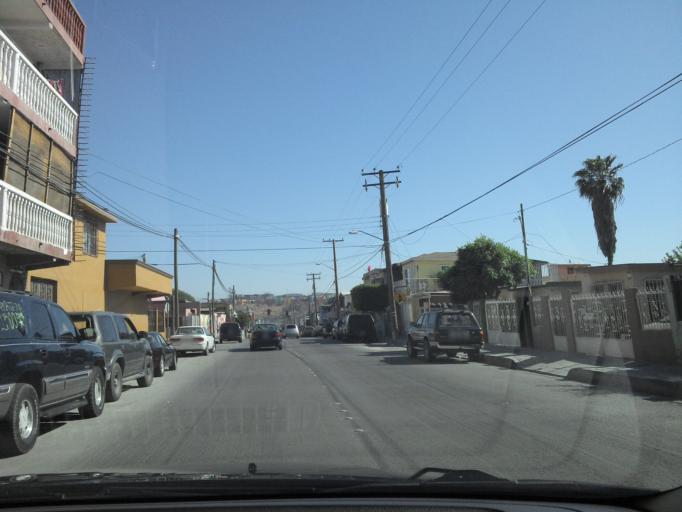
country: MX
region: Baja California
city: Tijuana
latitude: 32.5251
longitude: -116.9276
